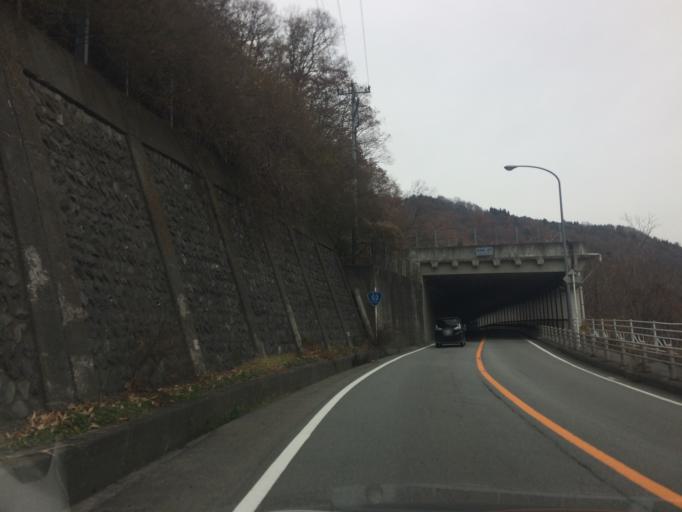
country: JP
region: Yamanashi
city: Ryuo
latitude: 35.5004
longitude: 138.4460
